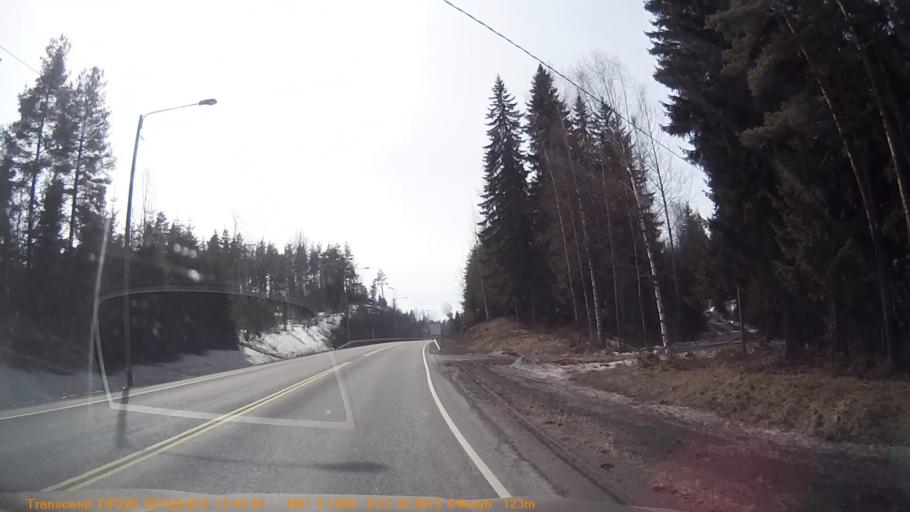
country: FI
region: Pirkanmaa
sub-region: Etelae-Pirkanmaa
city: Urjala
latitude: 61.0858
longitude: 23.5495
